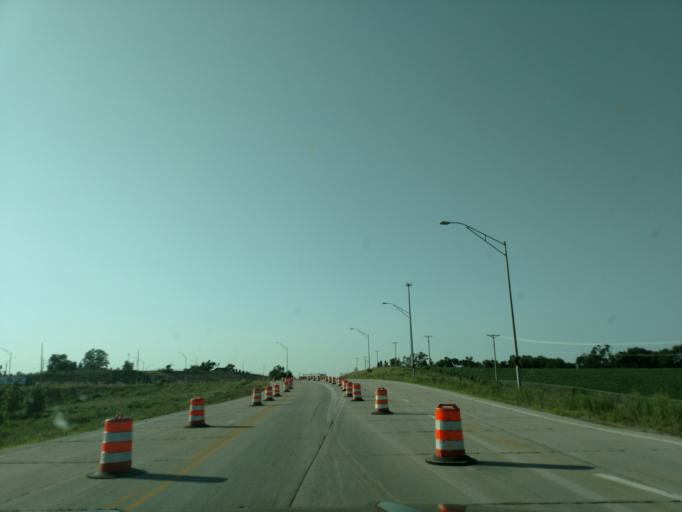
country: US
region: Nebraska
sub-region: Sarpy County
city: Offutt Air Force Base
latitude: 41.0827
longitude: -95.9262
